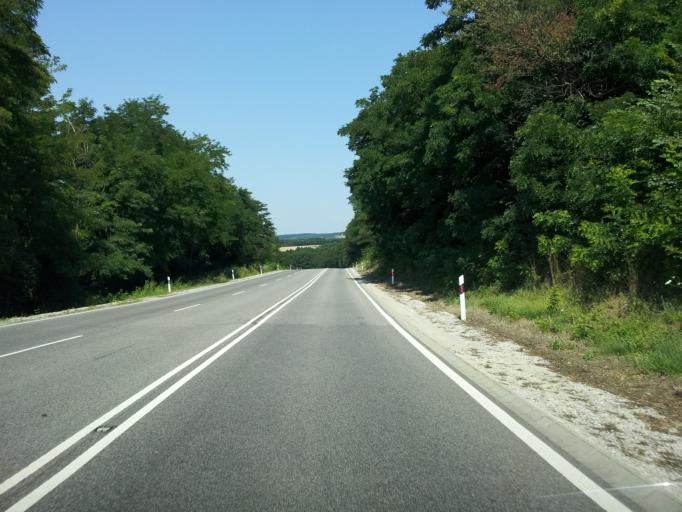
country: HU
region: Zala
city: Zalaegerszeg
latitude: 46.8268
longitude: 16.9565
